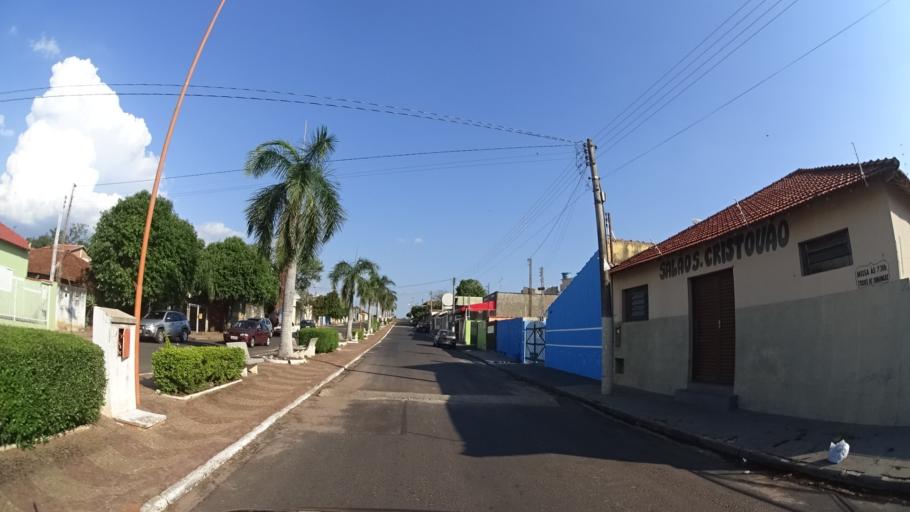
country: BR
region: Sao Paulo
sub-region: Urupes
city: Urupes
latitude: -21.3622
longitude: -49.4827
